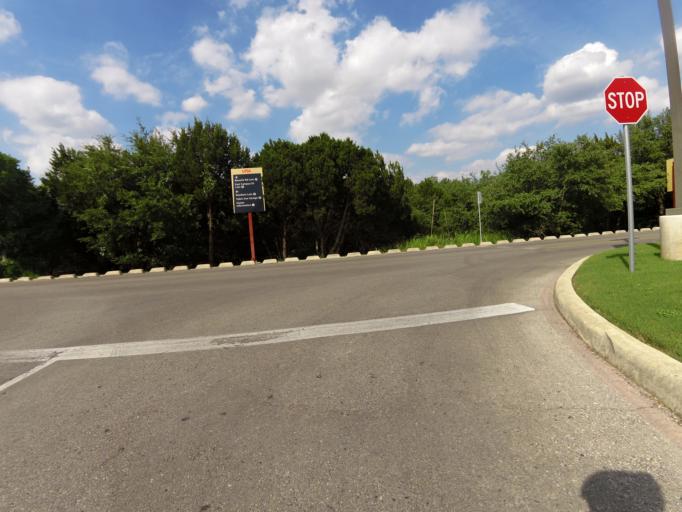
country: US
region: Texas
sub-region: Bexar County
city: Shavano Park
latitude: 29.5867
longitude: -98.6172
